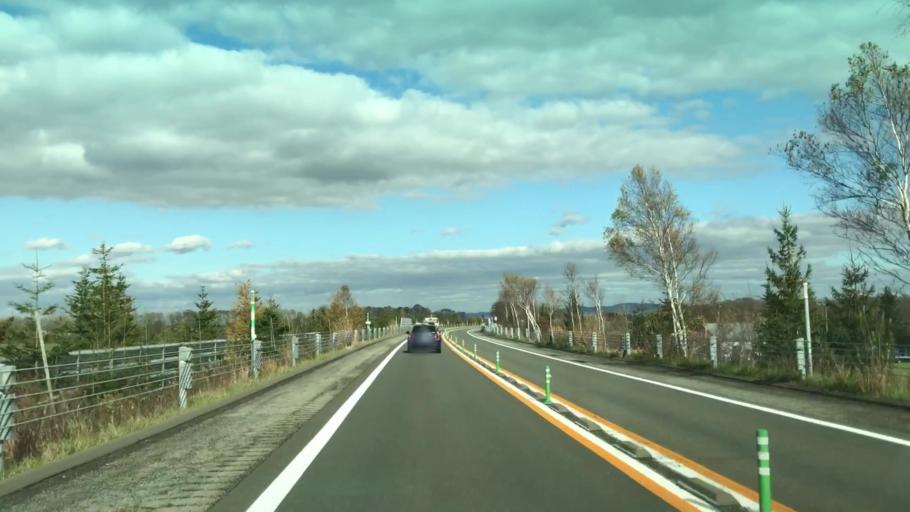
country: JP
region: Hokkaido
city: Chitose
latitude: 42.8793
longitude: 141.6188
